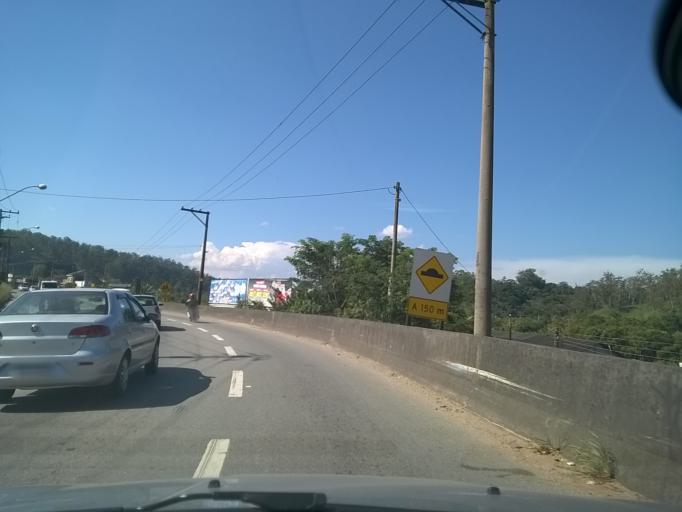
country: BR
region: Sao Paulo
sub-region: Caieiras
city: Caieiras
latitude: -23.3479
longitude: -46.7425
